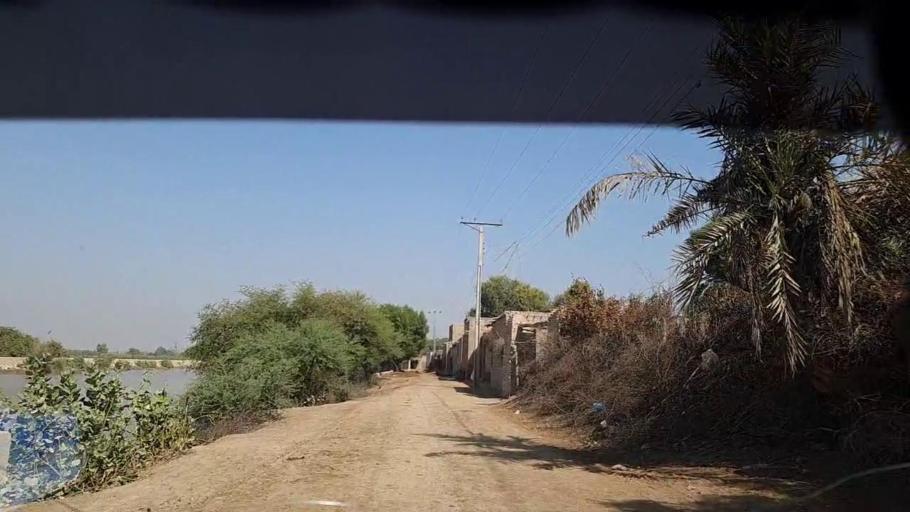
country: PK
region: Sindh
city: Naudero
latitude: 27.6677
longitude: 68.3777
